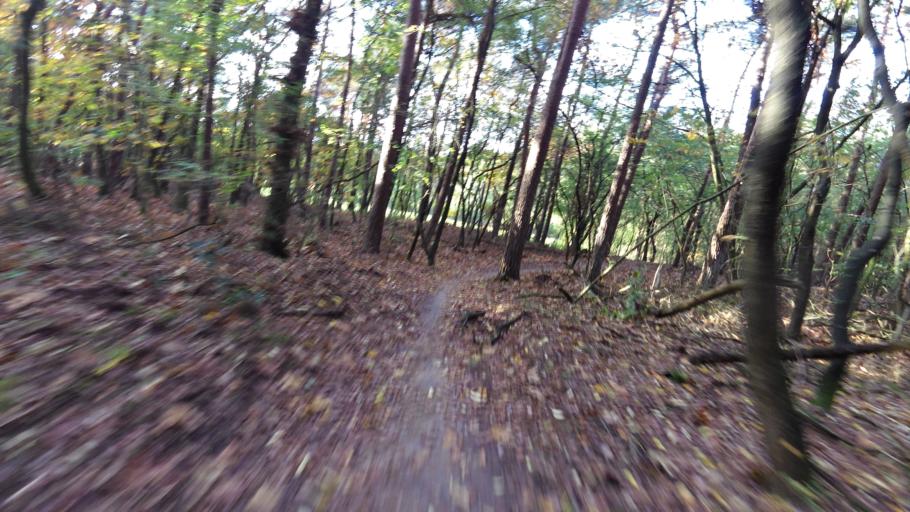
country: NL
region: Gelderland
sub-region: Gemeente Ede
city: Ede
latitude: 52.0705
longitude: 5.6616
